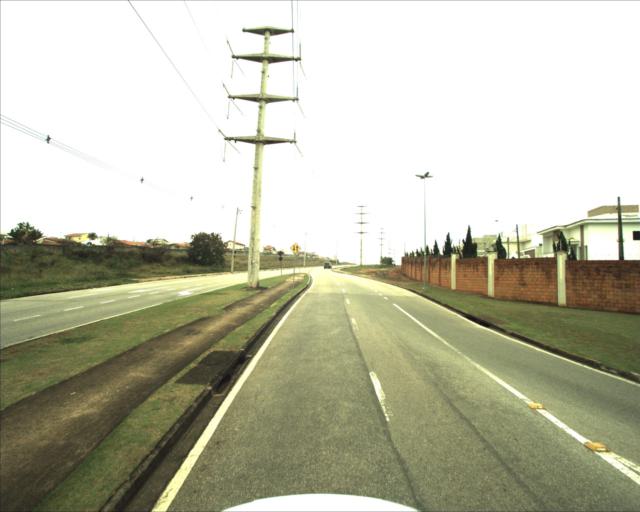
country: BR
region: Sao Paulo
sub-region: Sorocaba
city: Sorocaba
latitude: -23.4451
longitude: -47.4537
